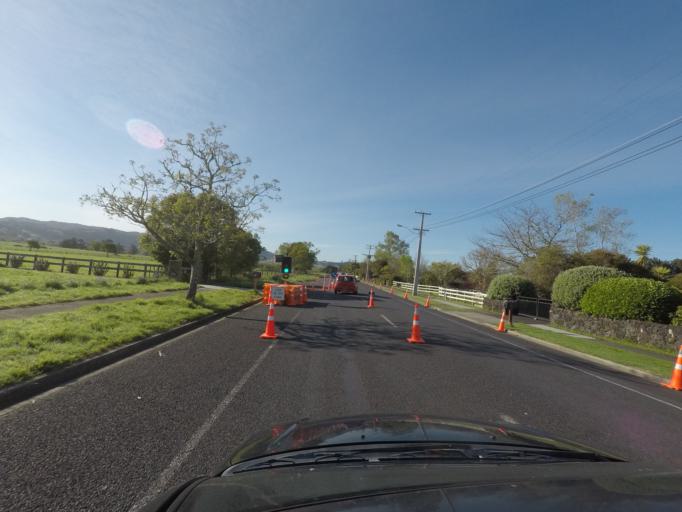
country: NZ
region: Auckland
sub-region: Auckland
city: Red Hill
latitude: -36.9982
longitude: 175.0384
